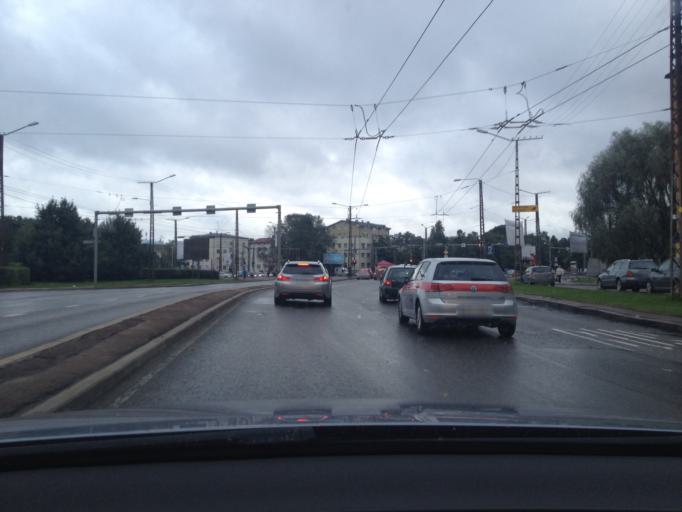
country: EE
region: Harju
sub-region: Tallinna linn
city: Tallinn
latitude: 59.4263
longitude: 24.7186
